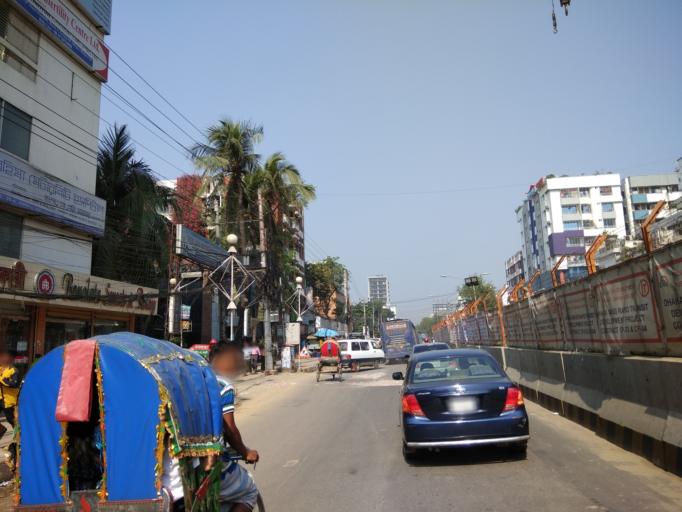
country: BD
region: Dhaka
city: Azimpur
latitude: 23.8096
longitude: 90.3678
